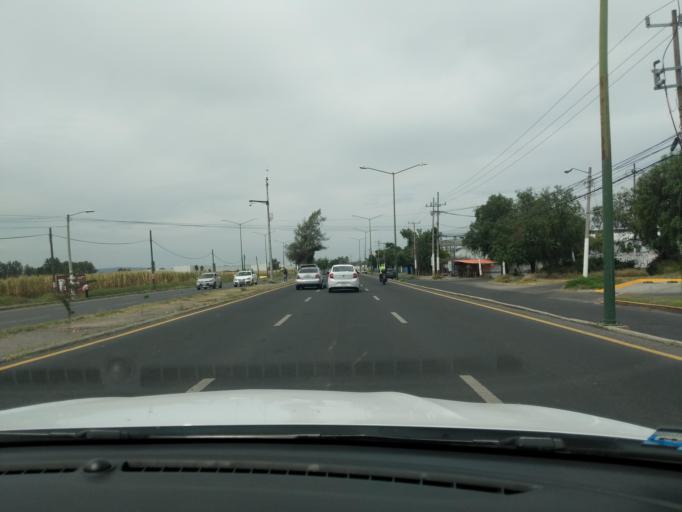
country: MX
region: Jalisco
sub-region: Zapopan
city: Puerta del Llano
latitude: 20.7884
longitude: -103.4723
